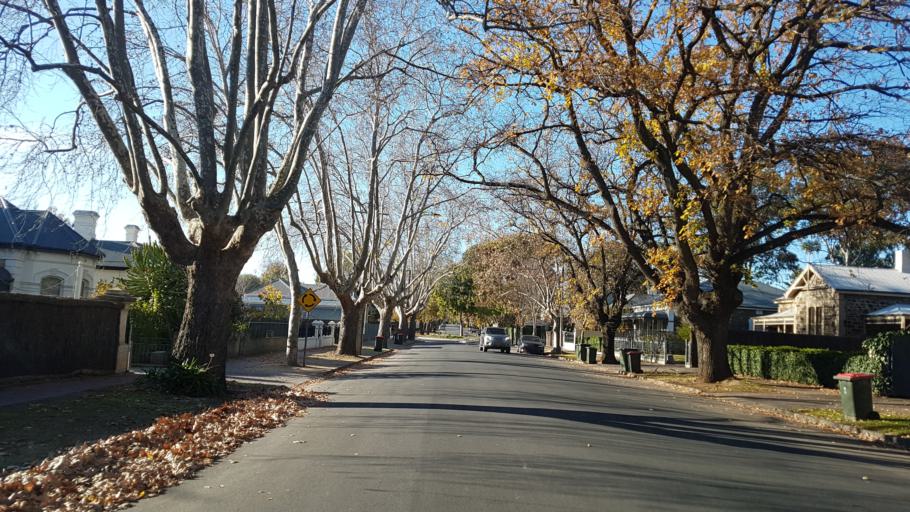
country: AU
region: South Australia
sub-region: Norwood Payneham St Peters
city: Royston Park
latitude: -34.9097
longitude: 138.6228
